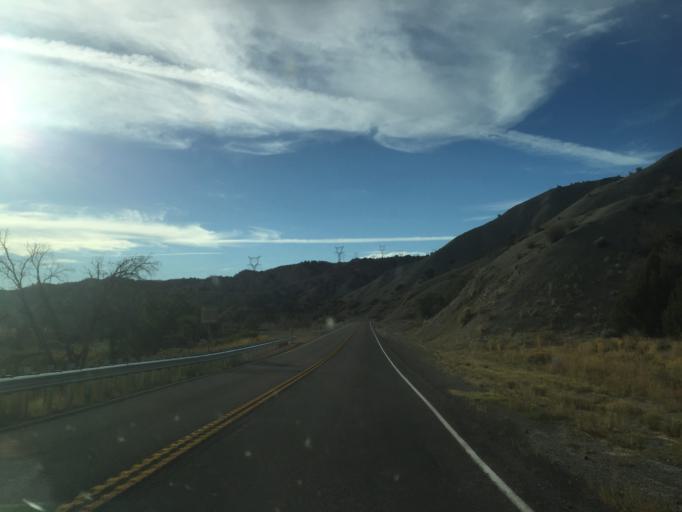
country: US
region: Utah
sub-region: Juab County
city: Nephi
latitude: 39.7181
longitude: -111.7541
